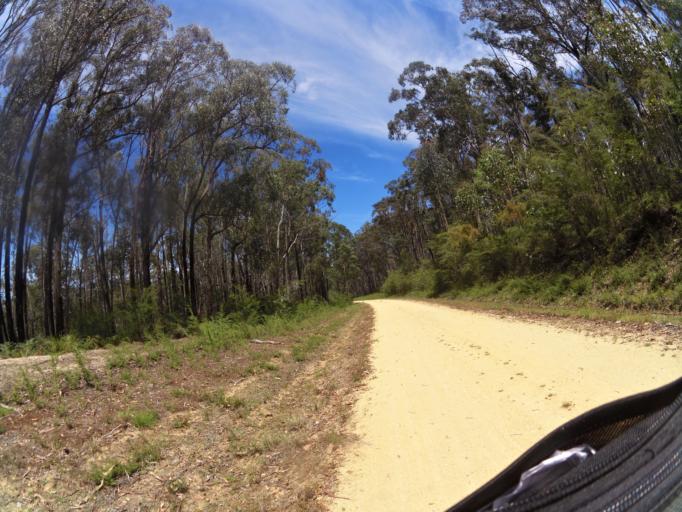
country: AU
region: Victoria
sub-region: East Gippsland
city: Lakes Entrance
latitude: -37.7315
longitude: 148.0821
